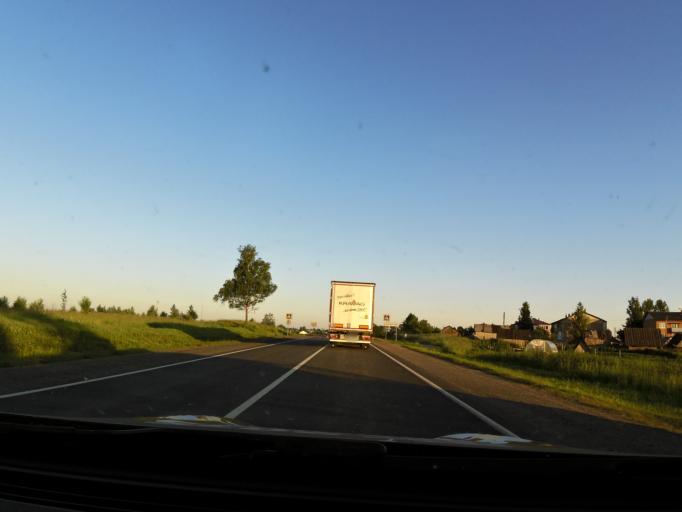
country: RU
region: Jaroslavl
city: Prechistoye
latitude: 58.4332
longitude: 40.3223
